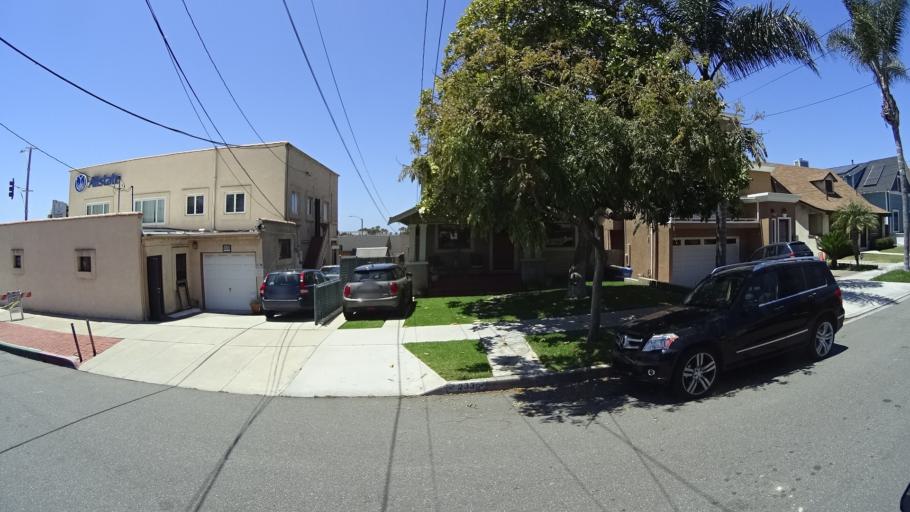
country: US
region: California
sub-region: Los Angeles County
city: Redondo Beach
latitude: 33.8384
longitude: -118.3842
